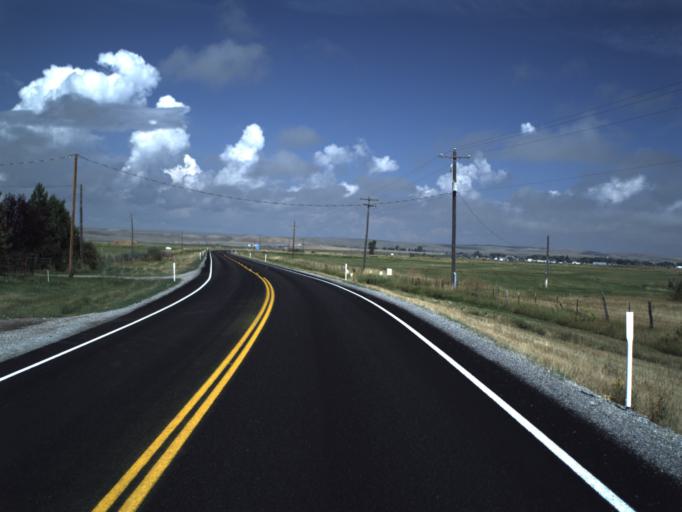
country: US
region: Utah
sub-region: Rich County
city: Randolph
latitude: 41.6369
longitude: -111.1796
